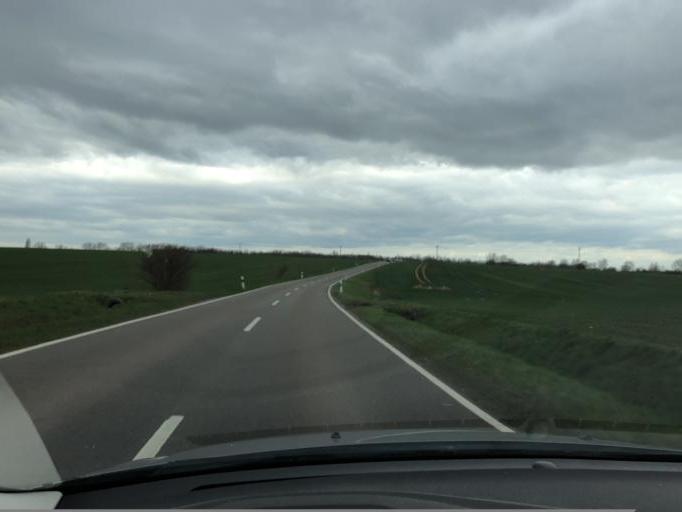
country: DE
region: Saxony-Anhalt
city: Hohenmolsen
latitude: 51.1517
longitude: 12.1286
